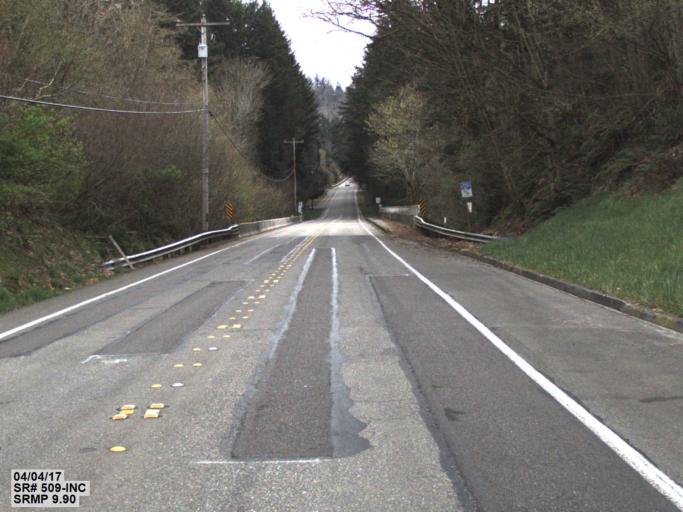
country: US
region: Washington
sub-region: King County
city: Federal Way
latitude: 47.3264
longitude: -122.3778
